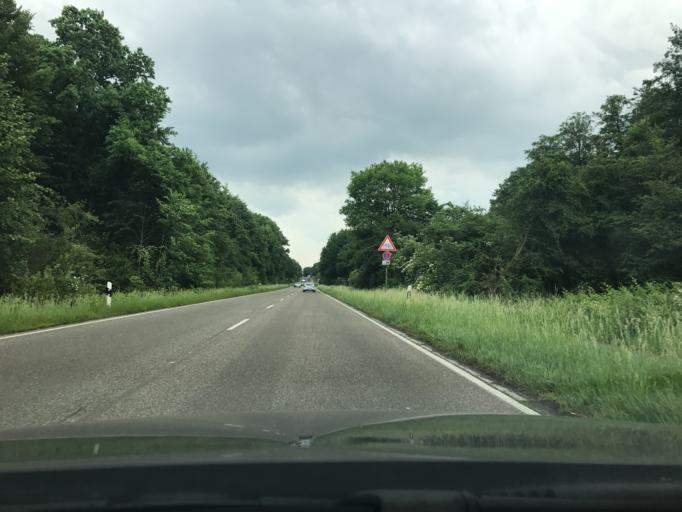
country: DE
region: North Rhine-Westphalia
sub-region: Regierungsbezirk Dusseldorf
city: Ratingen
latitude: 51.3026
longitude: 6.7953
